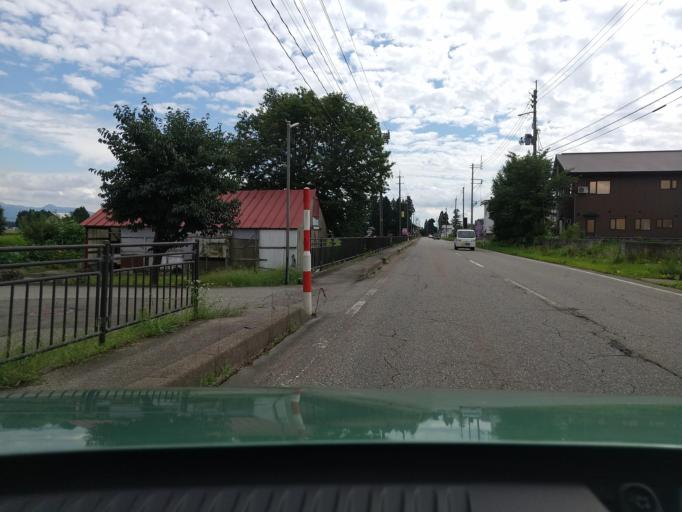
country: JP
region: Akita
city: Kakunodatemachi
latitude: 39.5641
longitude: 140.5591
